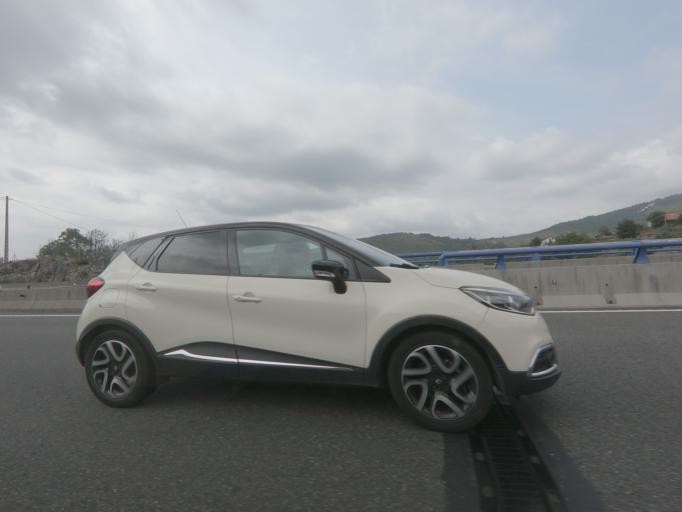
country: ES
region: Galicia
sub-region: Provincia de Pontevedra
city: Covelo
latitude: 42.1649
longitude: -8.3879
